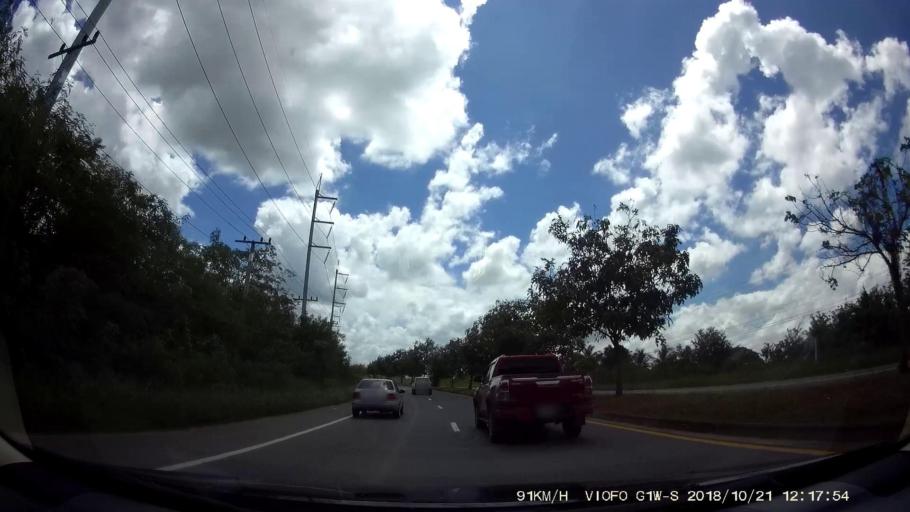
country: TH
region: Nakhon Ratchasima
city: Dan Khun Thot
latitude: 15.3250
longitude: 101.8181
